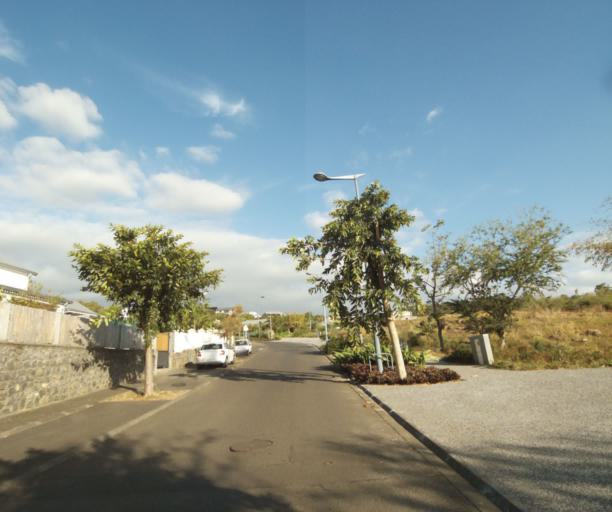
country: RE
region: Reunion
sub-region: Reunion
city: Saint-Paul
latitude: -21.0477
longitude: 55.2589
